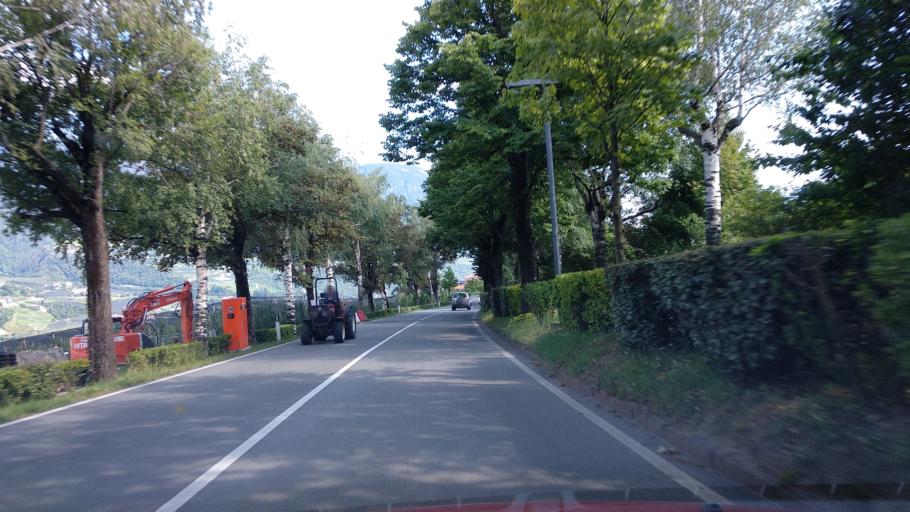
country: IT
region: Trentino-Alto Adige
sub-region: Bolzano
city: Tirolo
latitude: 46.6854
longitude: 11.1595
